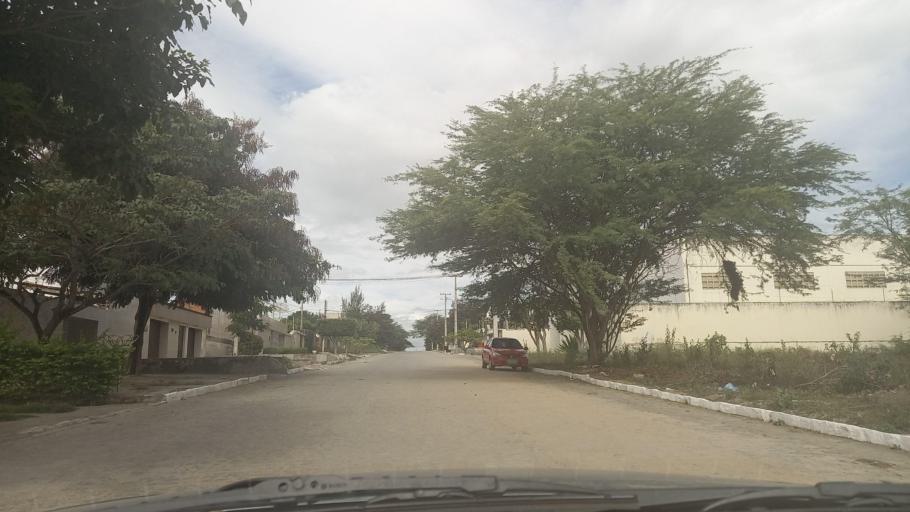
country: BR
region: Pernambuco
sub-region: Caruaru
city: Caruaru
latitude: -8.2945
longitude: -35.9914
